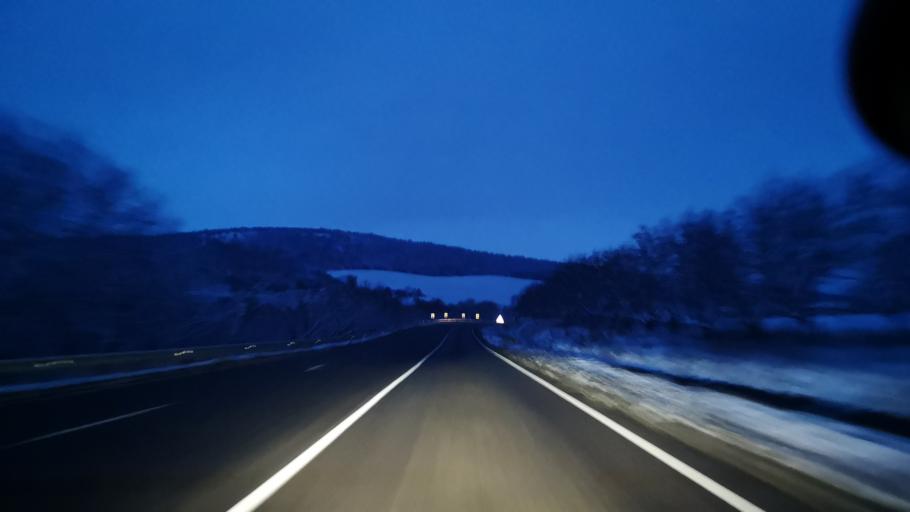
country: MD
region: Orhei
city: Orhei
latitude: 47.5103
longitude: 28.8013
